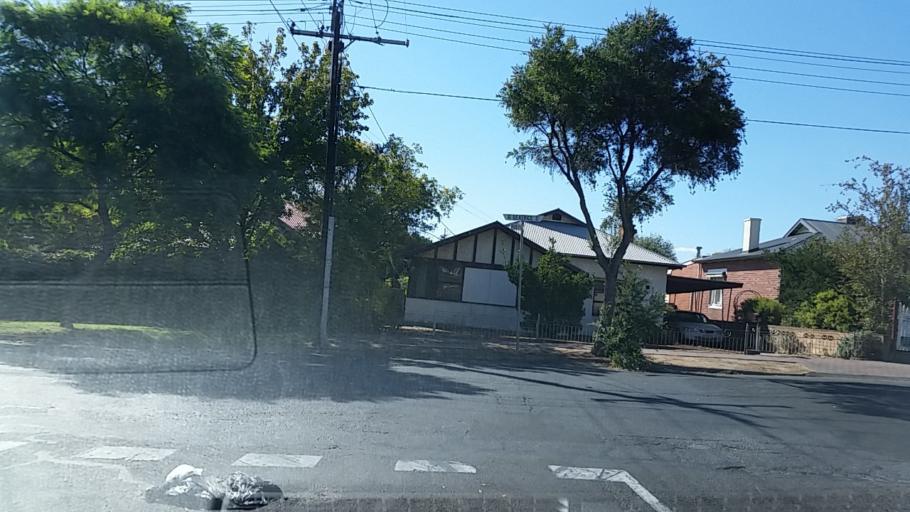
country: AU
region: South Australia
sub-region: Prospect
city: Prospect
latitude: -34.8816
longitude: 138.5891
